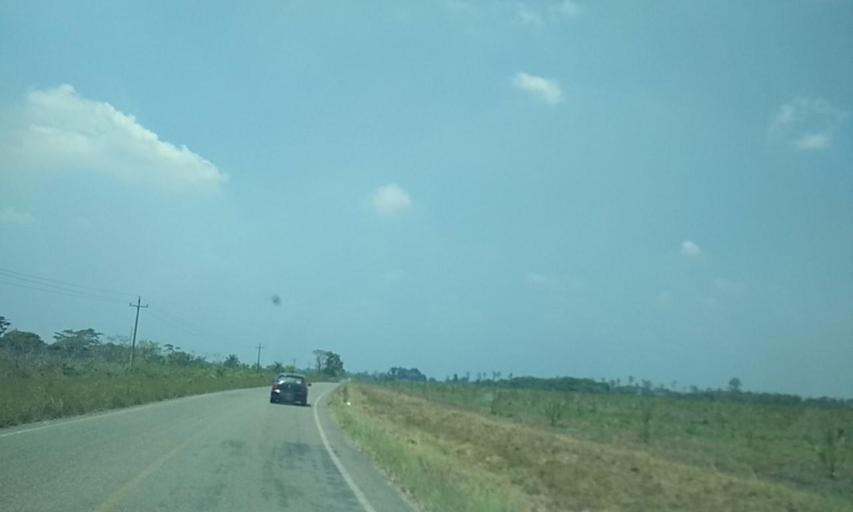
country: MX
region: Tabasco
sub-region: Huimanguillo
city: Paso de la Mina 3ra. Seccion
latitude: 17.8264
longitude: -93.6174
